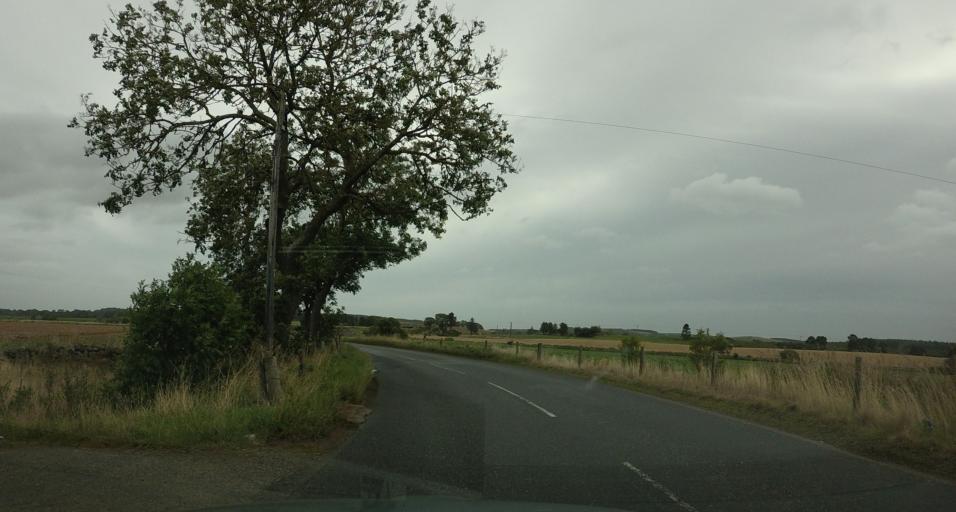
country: GB
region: Scotland
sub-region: Aberdeenshire
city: Kemnay
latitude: 57.2217
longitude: -2.4772
